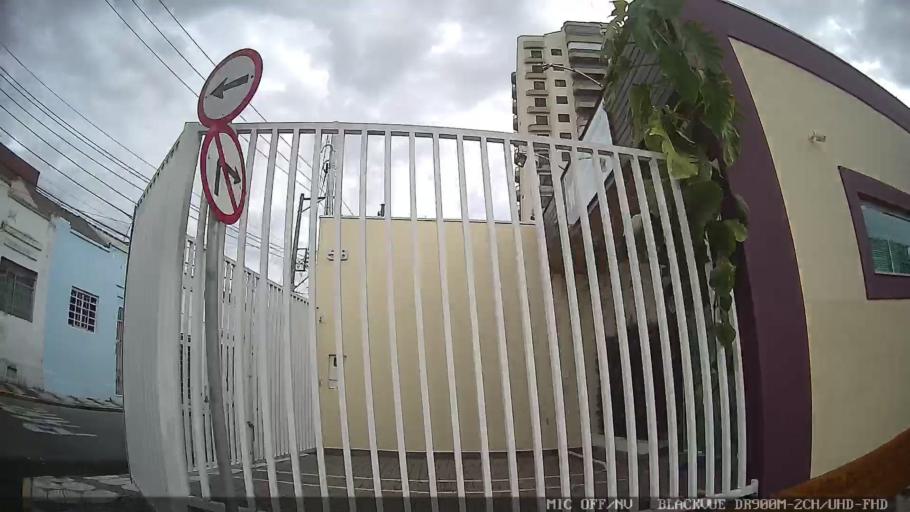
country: BR
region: Sao Paulo
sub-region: Mogi das Cruzes
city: Mogi das Cruzes
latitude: -23.5201
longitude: -46.1934
